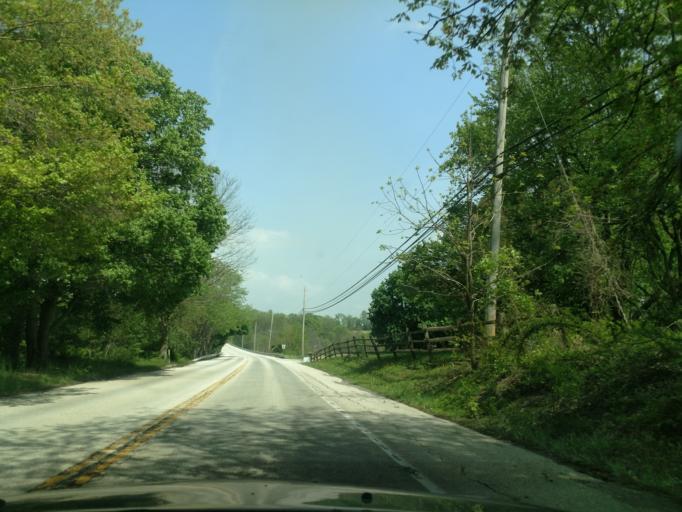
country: US
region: Pennsylvania
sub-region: Chester County
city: Elverson
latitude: 40.1570
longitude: -75.8188
